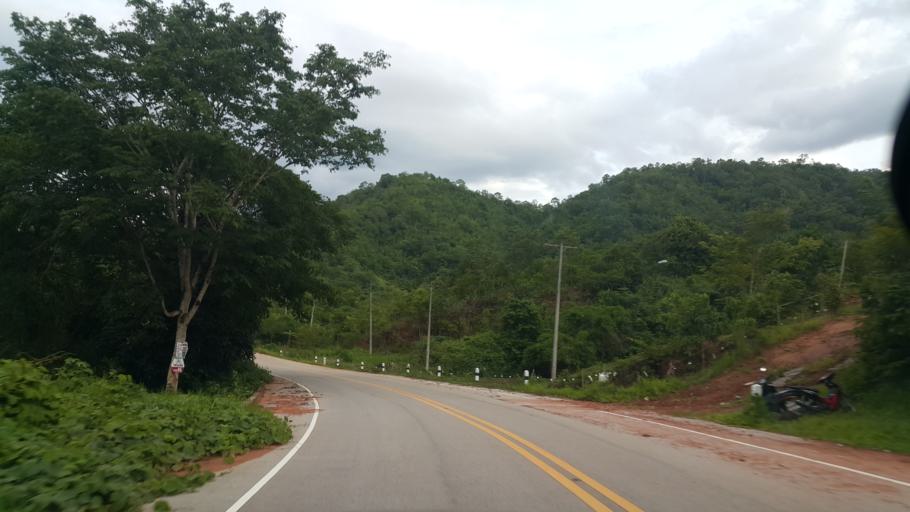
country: TH
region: Loei
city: Na Haeo
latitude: 17.4951
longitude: 101.0935
